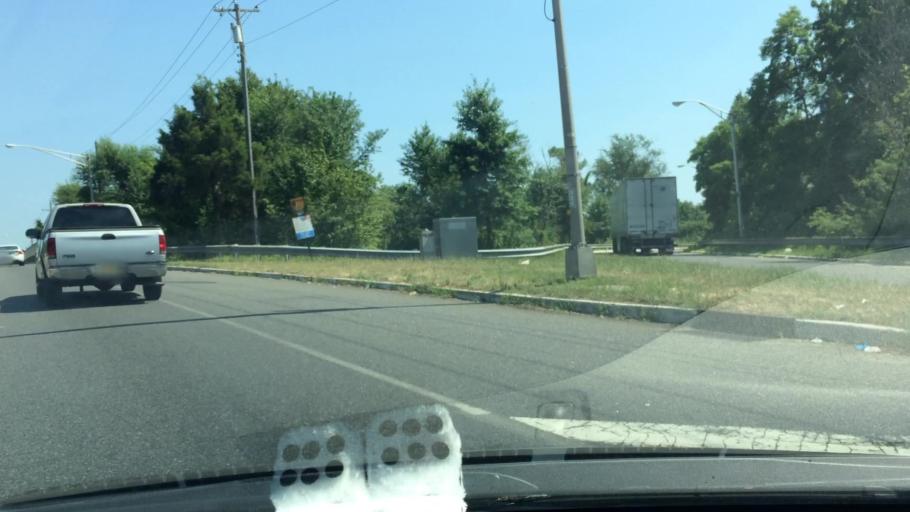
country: US
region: New Jersey
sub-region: Gloucester County
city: Beckett
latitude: 39.7627
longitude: -75.3621
